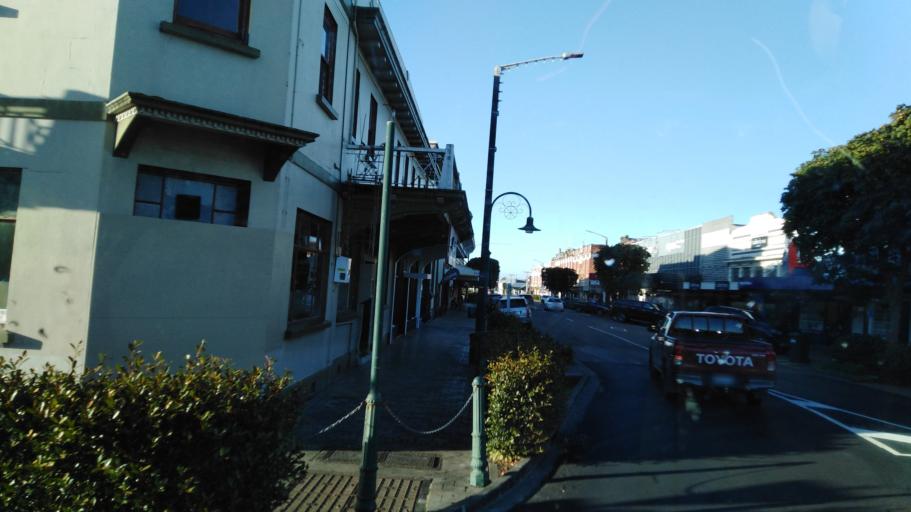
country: NZ
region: Manawatu-Wanganui
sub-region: Rangitikei District
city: Bulls
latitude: -40.0674
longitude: 175.3788
